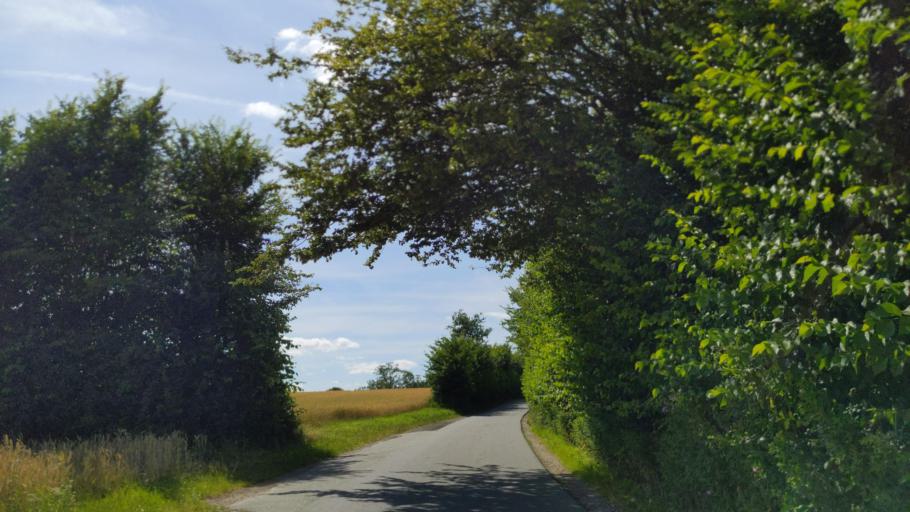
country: DE
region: Schleswig-Holstein
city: Beschendorf
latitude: 54.1601
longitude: 10.8551
